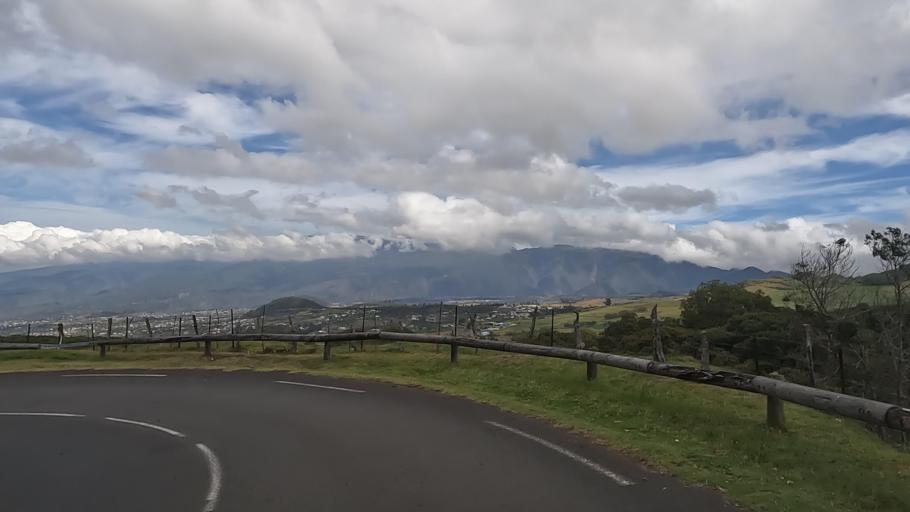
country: RE
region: Reunion
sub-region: Reunion
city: Le Tampon
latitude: -21.2437
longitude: 55.5901
